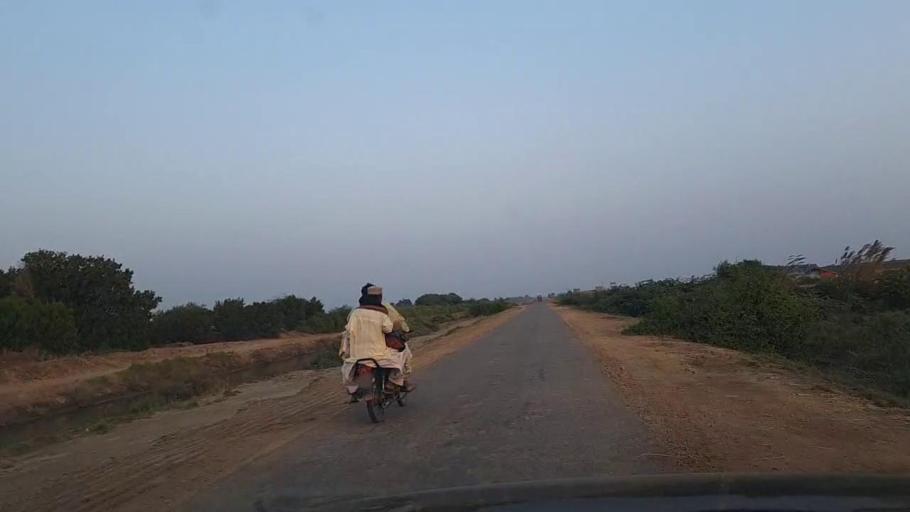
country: PK
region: Sindh
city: Mirpur Sakro
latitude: 24.6360
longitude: 67.6035
